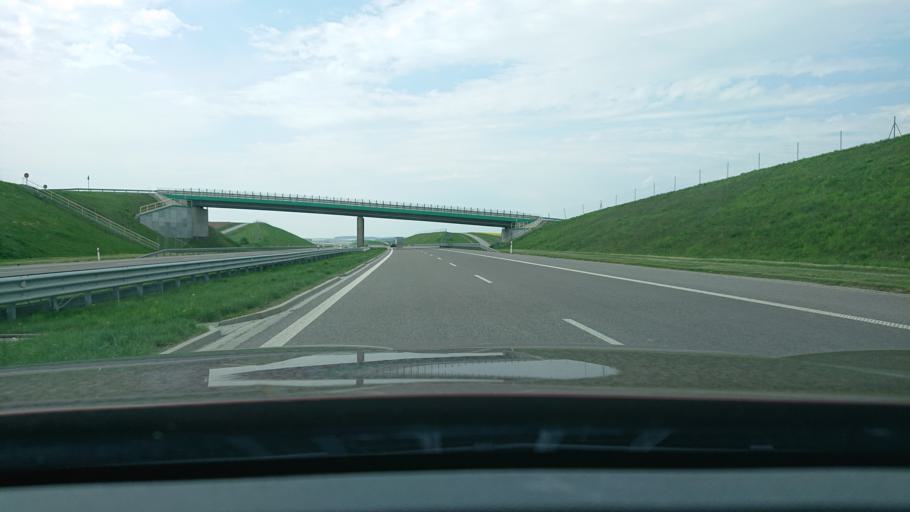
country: PL
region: Subcarpathian Voivodeship
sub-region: Powiat jaroslawski
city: Ostrow
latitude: 49.9301
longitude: 22.7171
